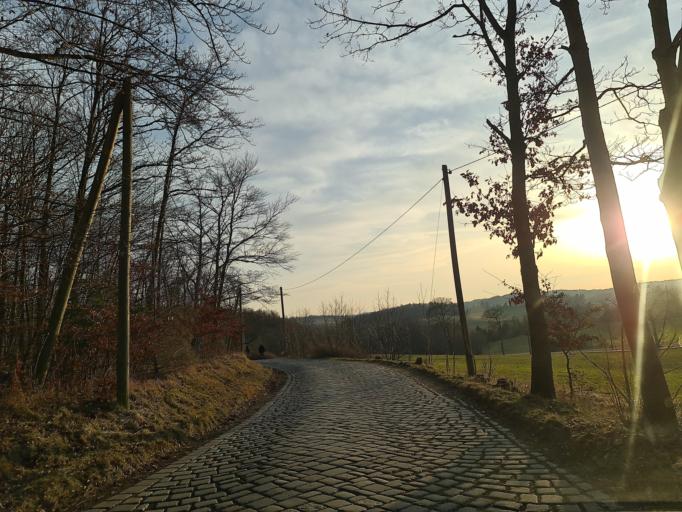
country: DE
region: Saxony
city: Plauen
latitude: 50.5152
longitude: 12.1126
